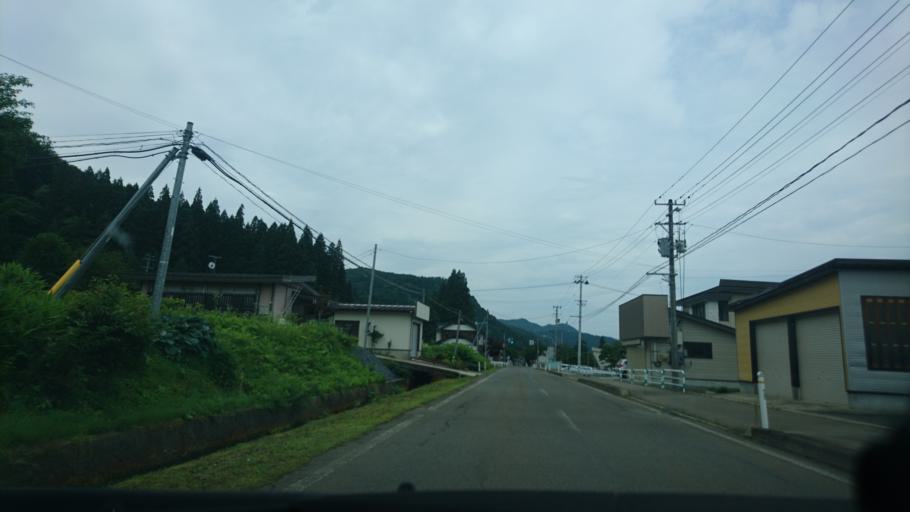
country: JP
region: Akita
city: Yuzawa
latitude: 39.1796
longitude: 140.6524
